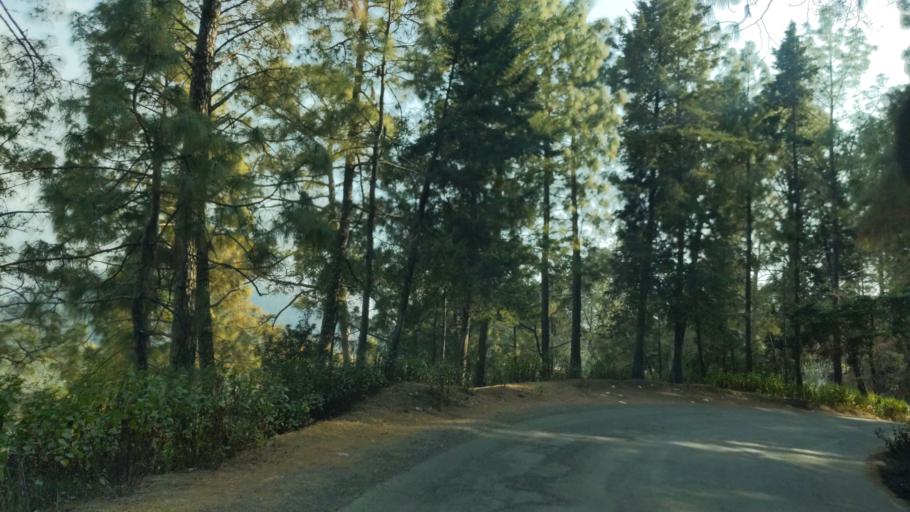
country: IN
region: Uttarakhand
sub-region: Naini Tal
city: Bhowali
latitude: 29.3903
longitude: 79.5399
